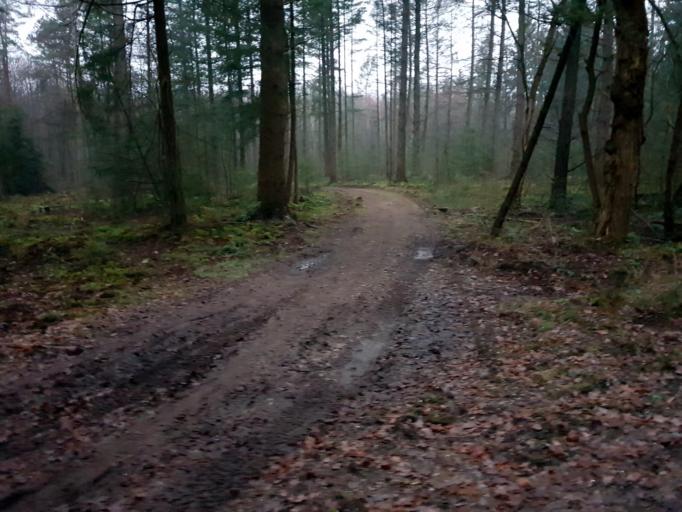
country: NL
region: Gelderland
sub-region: Gemeente Barneveld
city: Garderen
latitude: 52.2331
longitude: 5.6825
